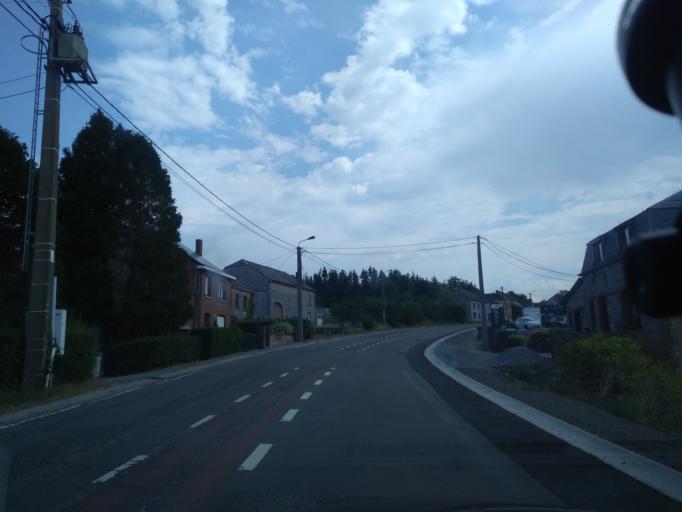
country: BE
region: Wallonia
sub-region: Province de Namur
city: Dinant
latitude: 50.1973
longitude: 4.8966
